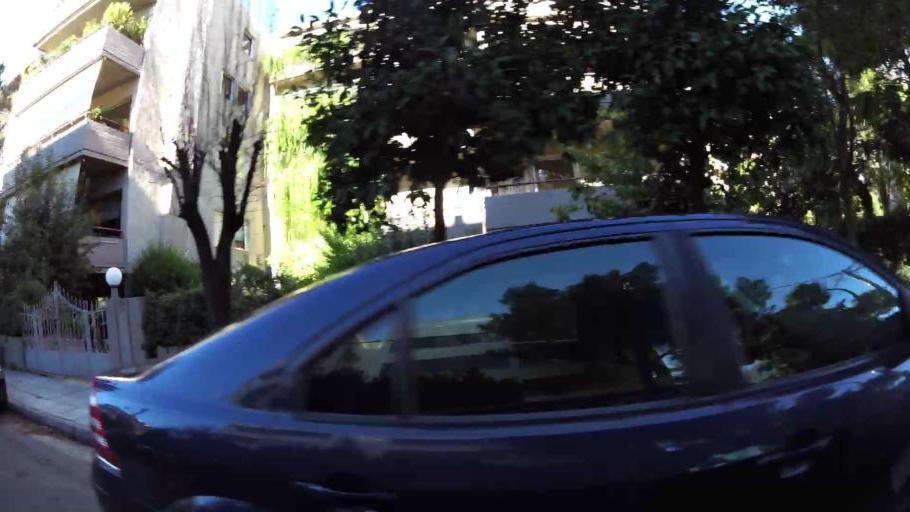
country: GR
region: Attica
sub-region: Nomarchia Athinas
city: Vrilissia
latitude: 38.0390
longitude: 23.8331
